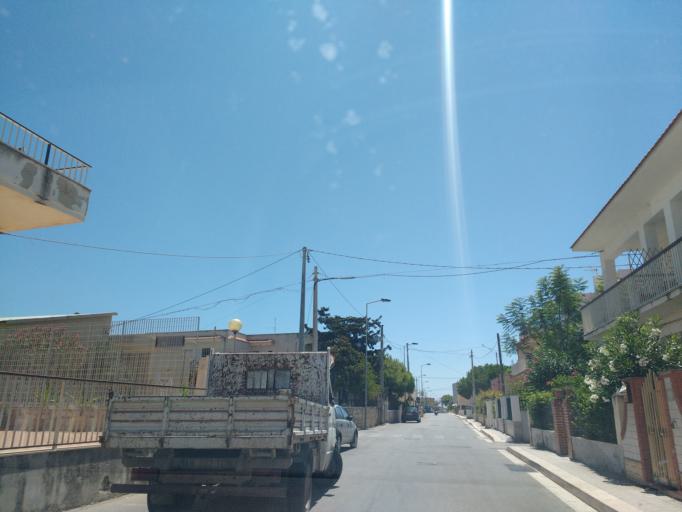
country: IT
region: Sicily
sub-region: Ragusa
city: Cava d'Aliga
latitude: 36.7260
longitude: 14.6894
